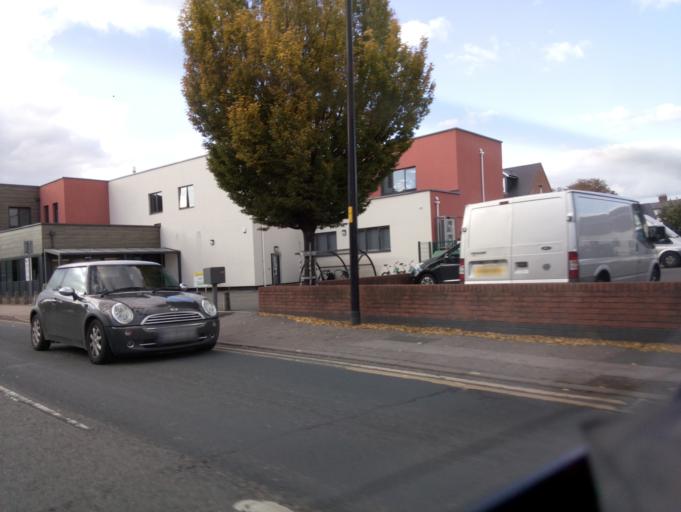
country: GB
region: England
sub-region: Herefordshire
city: Hereford
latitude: 52.0583
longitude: -2.7141
